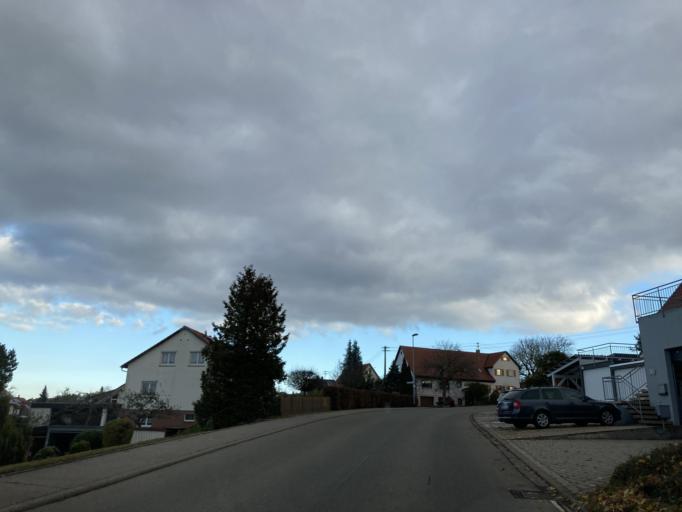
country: DE
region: Baden-Wuerttemberg
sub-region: Tuebingen Region
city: Haigerloch
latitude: 48.4341
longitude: 8.7815
